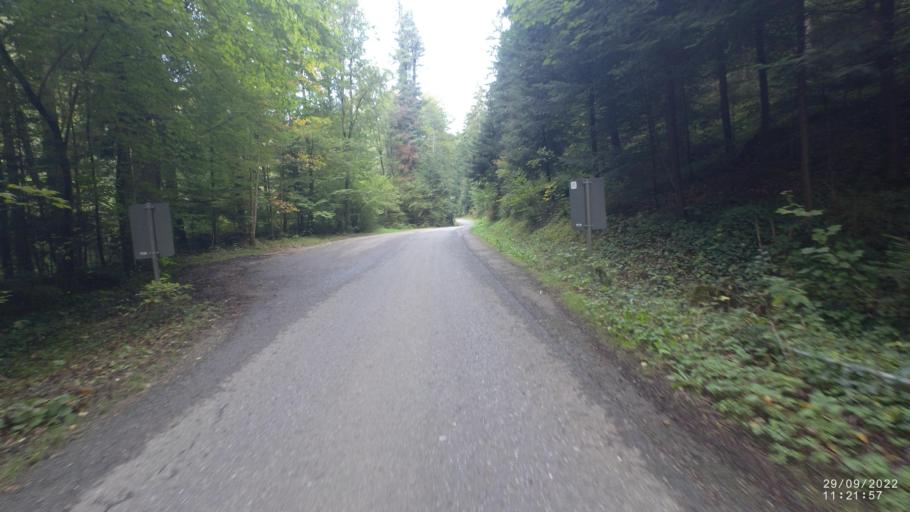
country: DE
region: Baden-Wuerttemberg
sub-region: Regierungsbezirk Stuttgart
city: Bortlingen
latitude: 48.7491
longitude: 9.6191
